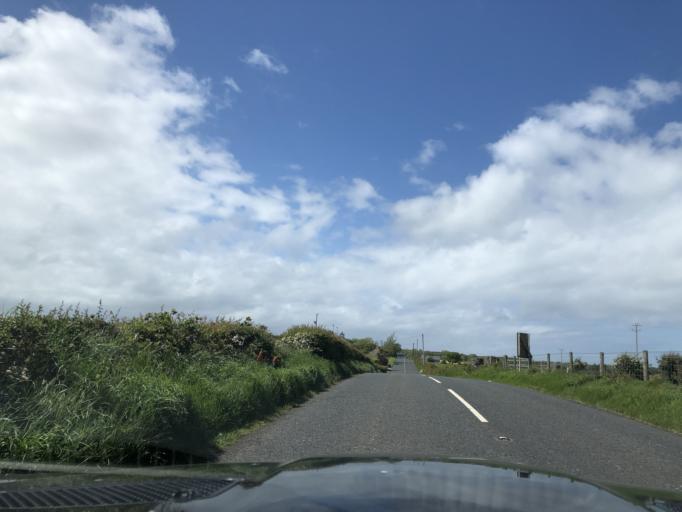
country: GB
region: Northern Ireland
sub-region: Moyle District
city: Ballycastle
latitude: 55.2140
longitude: -6.2813
